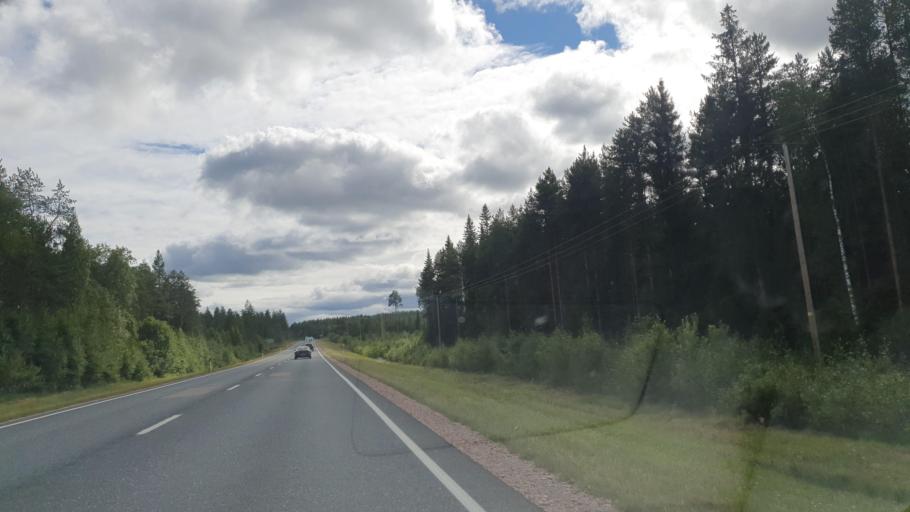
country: FI
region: Kainuu
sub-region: Kajaani
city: Kajaani
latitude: 64.1033
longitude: 27.4487
